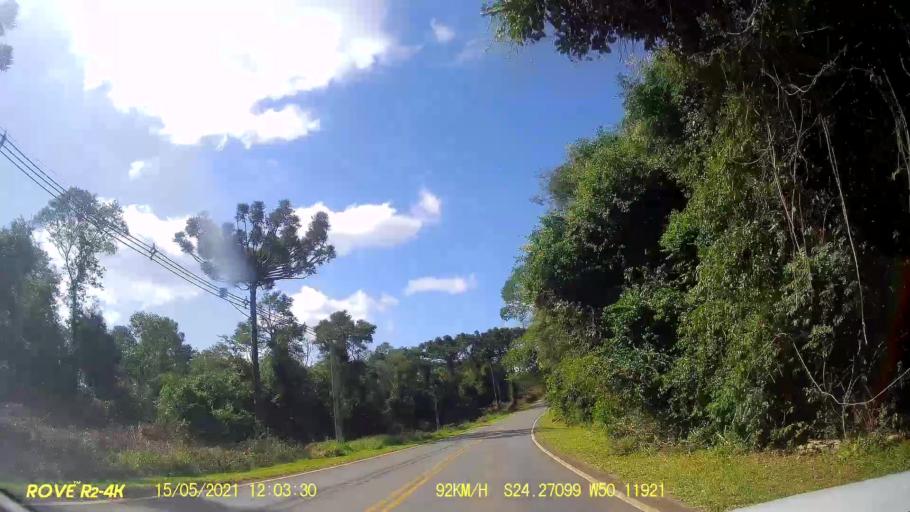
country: BR
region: Parana
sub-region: Pirai Do Sul
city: Pirai do Sul
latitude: -24.2710
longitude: -50.1193
